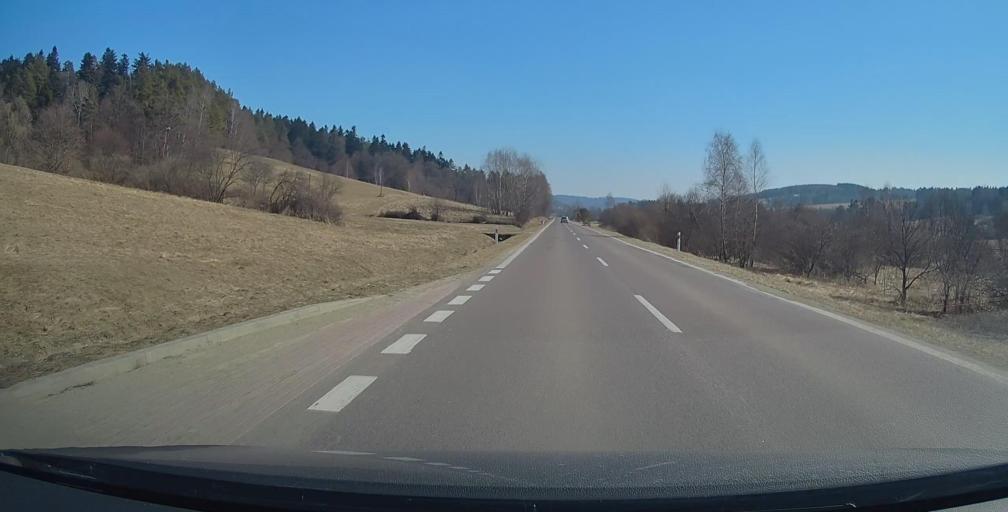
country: PL
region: Subcarpathian Voivodeship
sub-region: Powiat przemyski
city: Bircza
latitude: 49.5942
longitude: 22.5173
